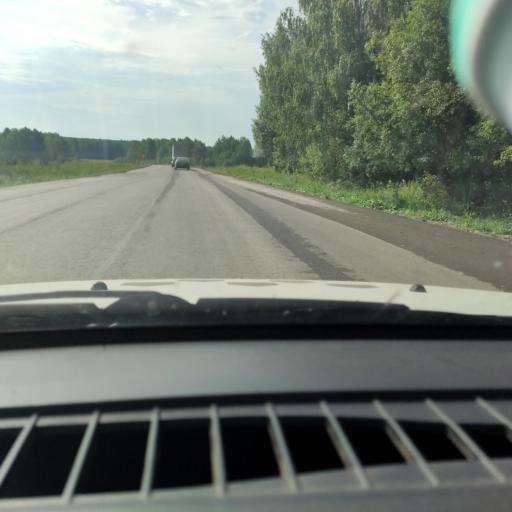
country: RU
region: Perm
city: Siva
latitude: 58.4607
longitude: 54.4082
